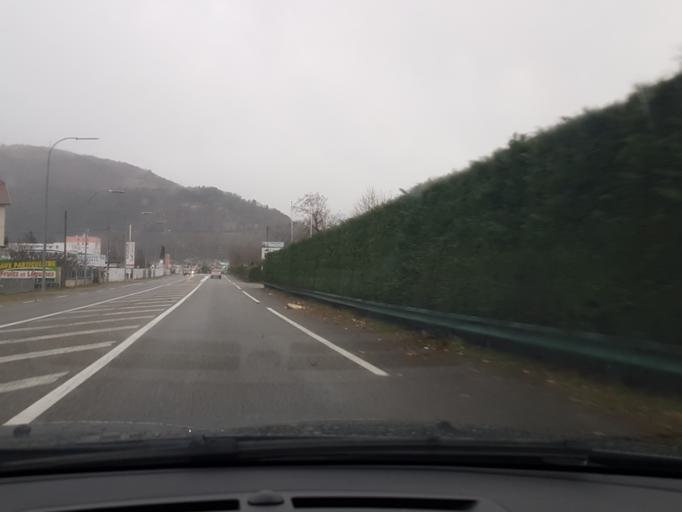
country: FR
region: Midi-Pyrenees
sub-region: Departement de l'Ariege
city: Foix
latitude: 42.9899
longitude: 1.6162
